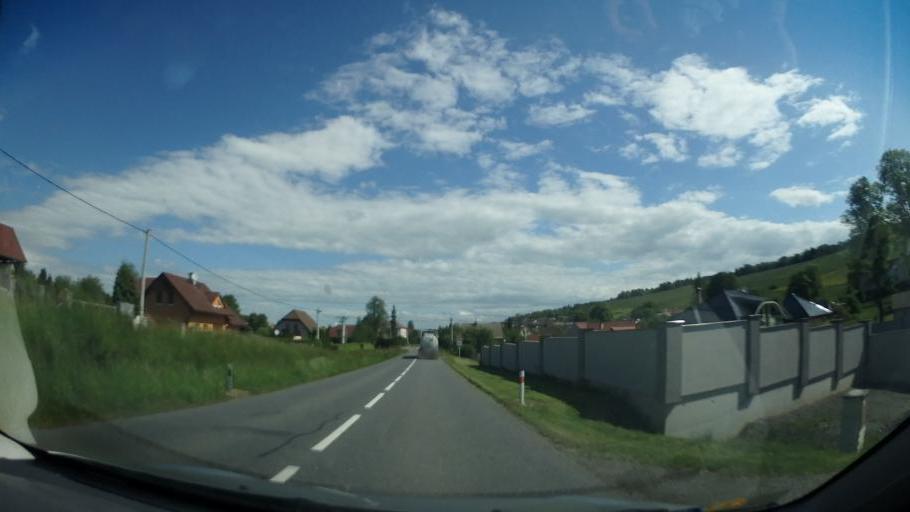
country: CZ
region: Pardubicky
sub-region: Okres Svitavy
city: Moravska Trebova
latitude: 49.7287
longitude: 16.6423
